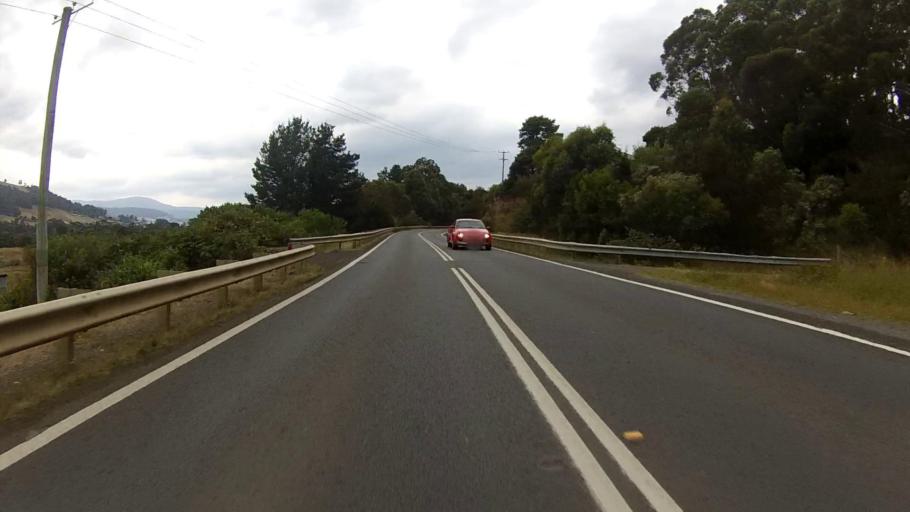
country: AU
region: Tasmania
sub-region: Huon Valley
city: Huonville
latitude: -43.0558
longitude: 147.0468
